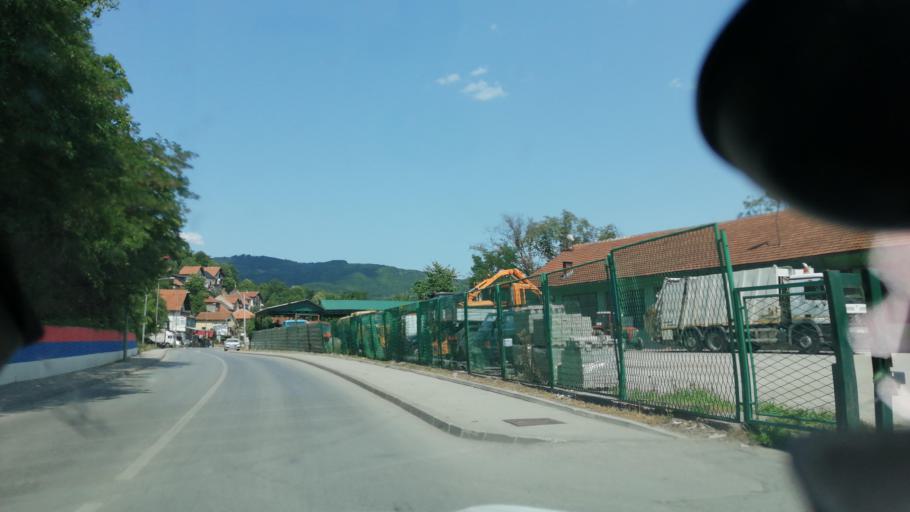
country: RS
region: Central Serbia
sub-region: Moravicki Okrug
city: Ivanjica
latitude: 43.5861
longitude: 20.2244
